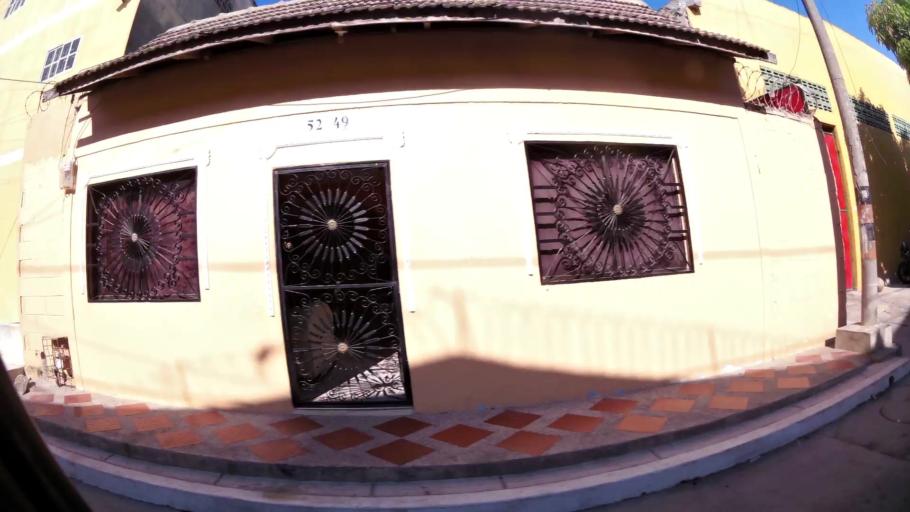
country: CO
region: Atlantico
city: Barranquilla
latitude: 10.9920
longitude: -74.7822
